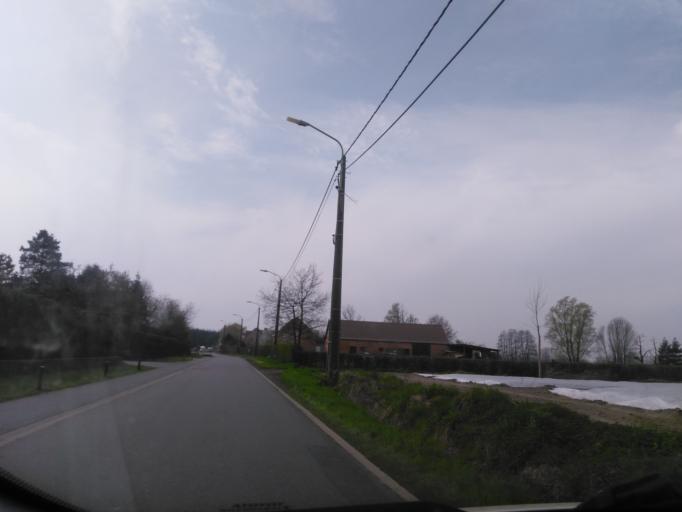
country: BE
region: Flanders
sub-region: Provincie Oost-Vlaanderen
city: Beveren
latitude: 51.2016
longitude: 4.2164
